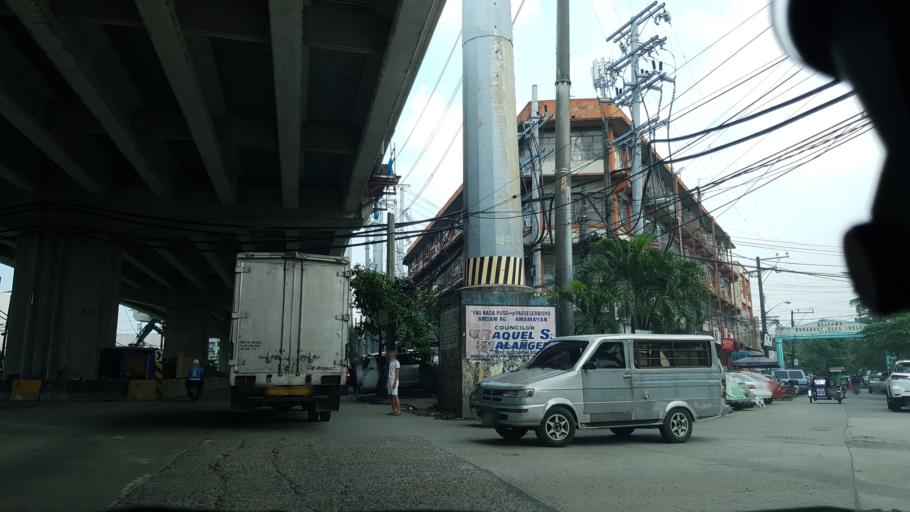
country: PH
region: Metro Manila
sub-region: San Juan
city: San Juan
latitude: 14.6170
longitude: 121.0160
